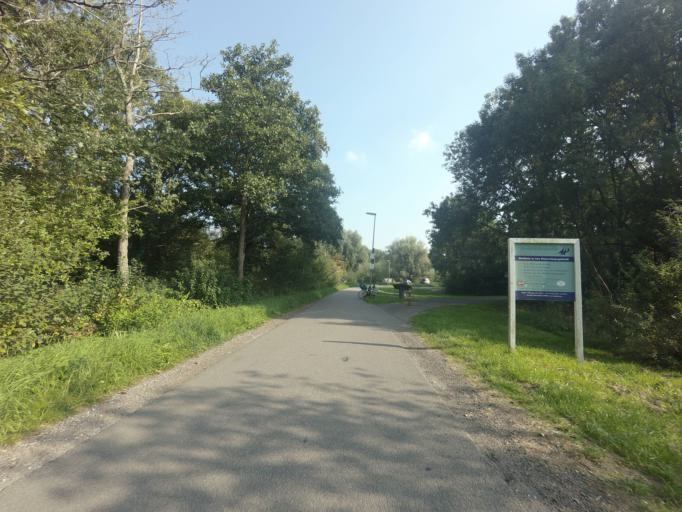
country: NL
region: Groningen
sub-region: Gemeente Groningen
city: Groningen
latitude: 53.1872
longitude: 6.5652
